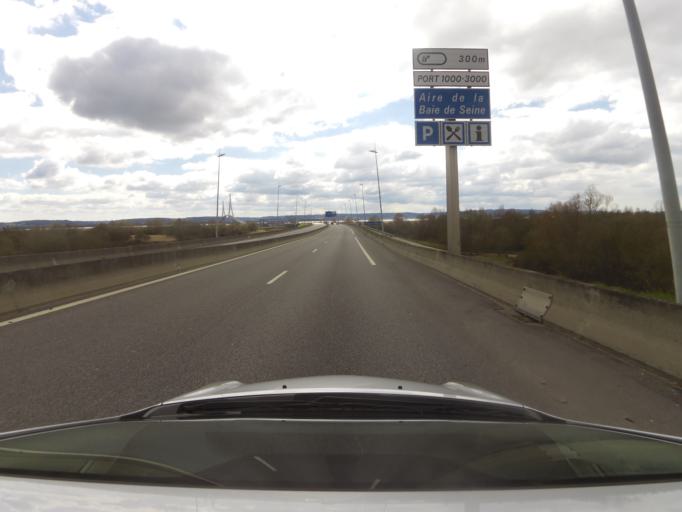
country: FR
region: Haute-Normandie
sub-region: Departement de la Seine-Maritime
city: Rogerville
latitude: 49.4582
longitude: 0.2731
